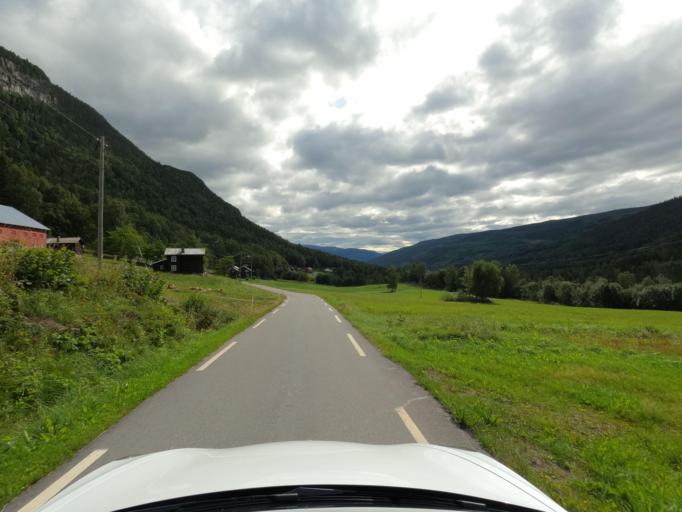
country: NO
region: Telemark
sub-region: Tinn
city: Rjukan
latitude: 60.0003
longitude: 8.6811
